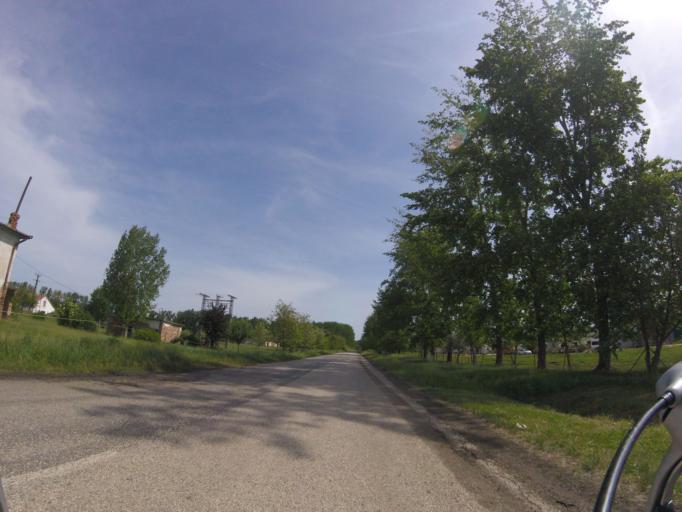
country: HU
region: Jasz-Nagykun-Szolnok
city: Tiszapuspoki
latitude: 47.2795
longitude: 20.3706
